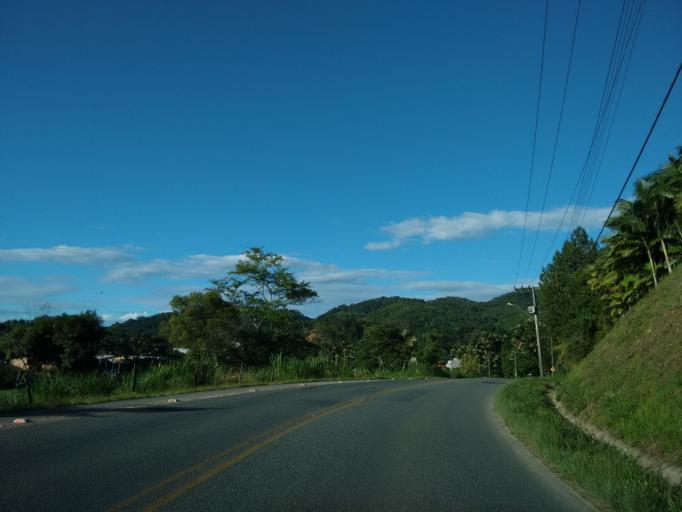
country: BR
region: Santa Catarina
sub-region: Pomerode
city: Pomerode
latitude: -26.7496
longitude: -49.1653
